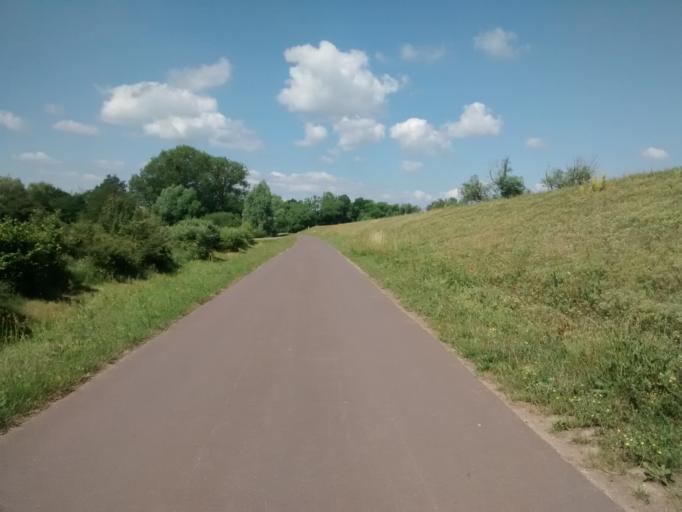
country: DE
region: Saxony-Anhalt
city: Wittenburg
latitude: 51.8470
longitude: 12.5936
